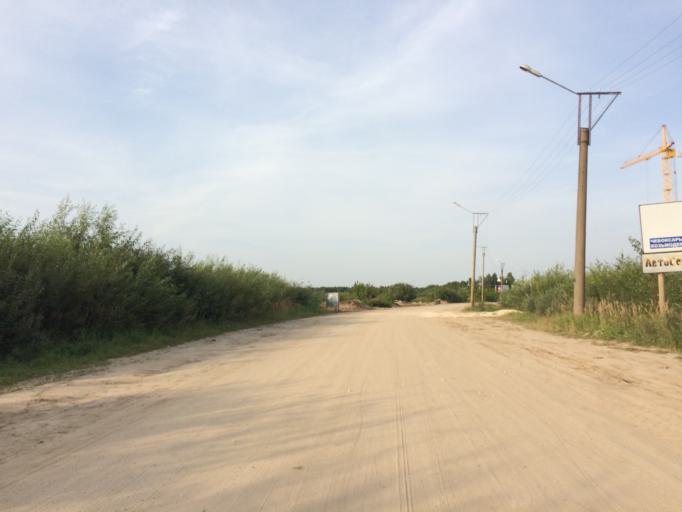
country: RU
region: Mariy-El
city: Yoshkar-Ola
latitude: 56.6421
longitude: 47.9212
